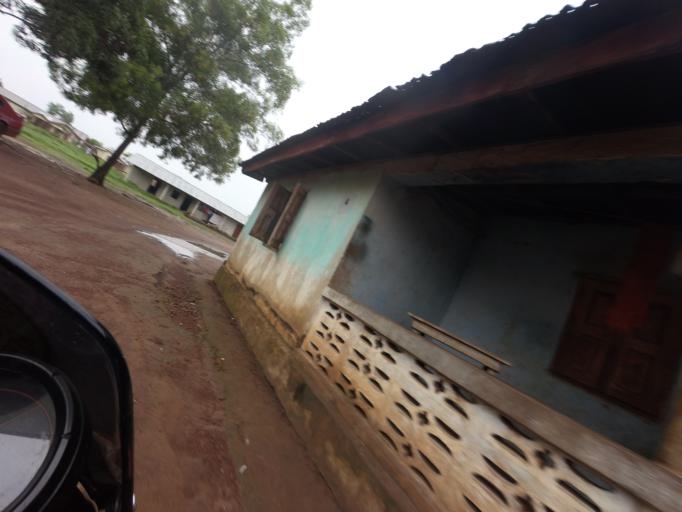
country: SL
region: Northern Province
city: Kambia
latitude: 9.1086
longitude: -12.9276
